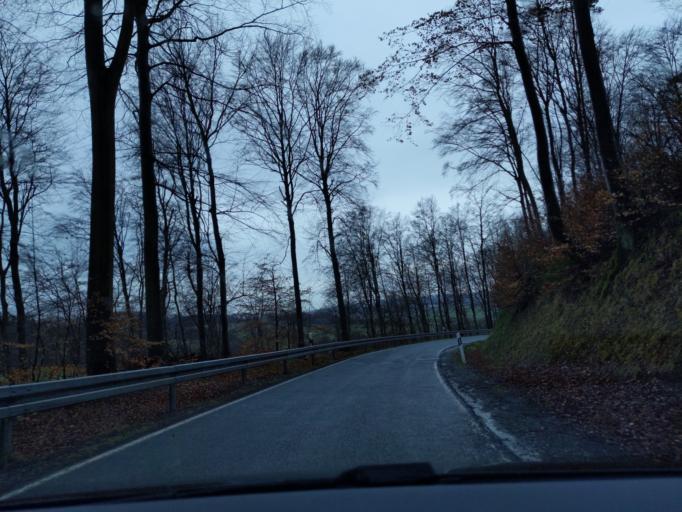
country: DE
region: Hesse
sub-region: Regierungsbezirk Kassel
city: Bad Arolsen
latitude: 51.3251
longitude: 9.0247
